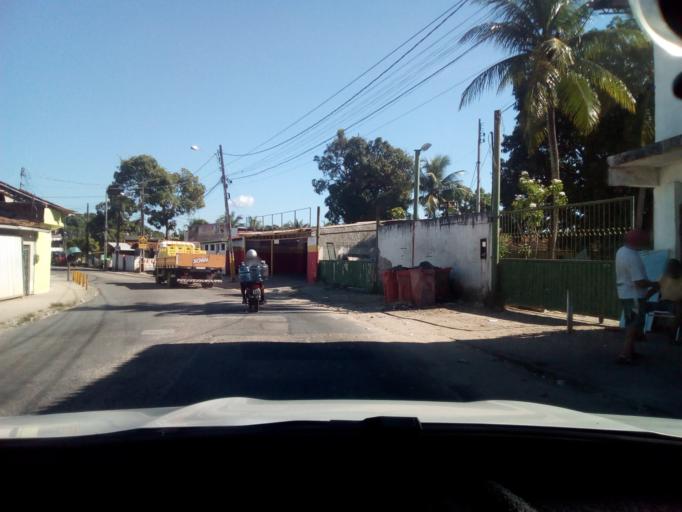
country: BR
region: Paraiba
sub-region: Joao Pessoa
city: Joao Pessoa
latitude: -7.1089
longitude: -34.8840
